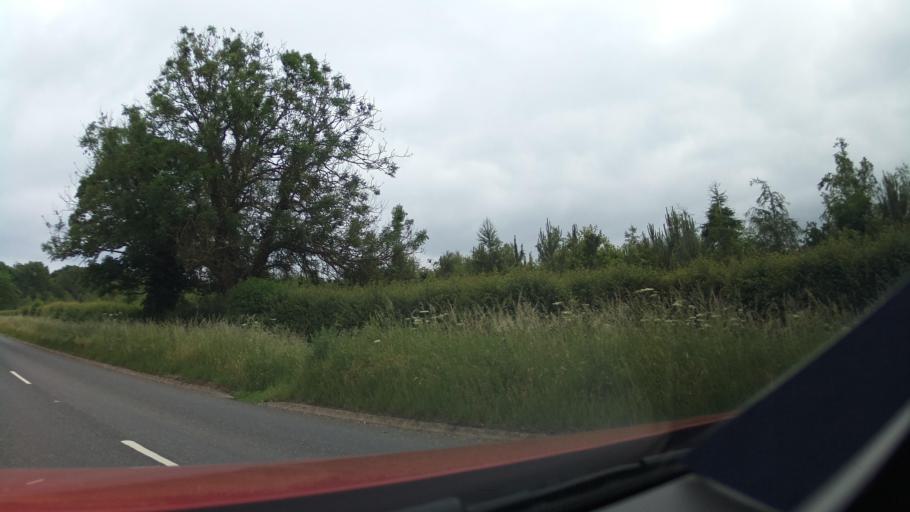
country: GB
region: England
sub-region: District of Rutland
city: Manton
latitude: 52.6249
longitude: -0.7104
